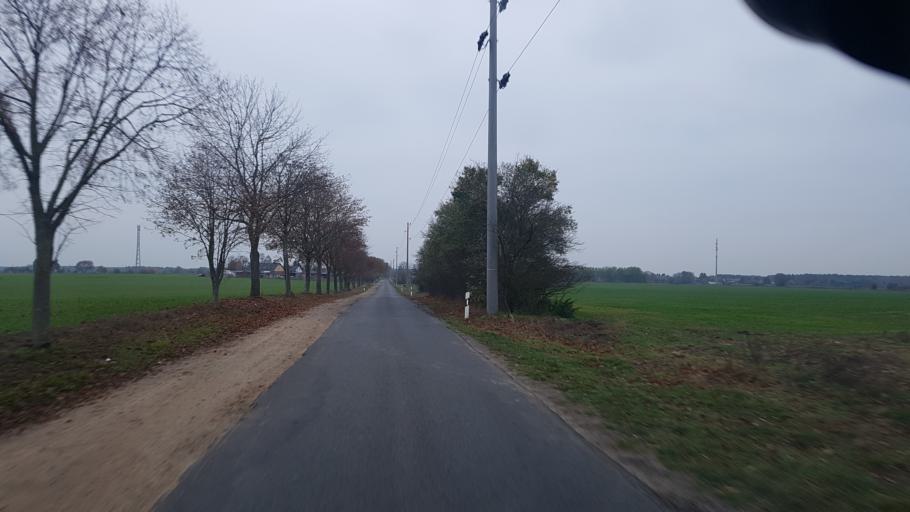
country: DE
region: Brandenburg
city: Ruthnick
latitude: 52.9112
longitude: 12.9830
